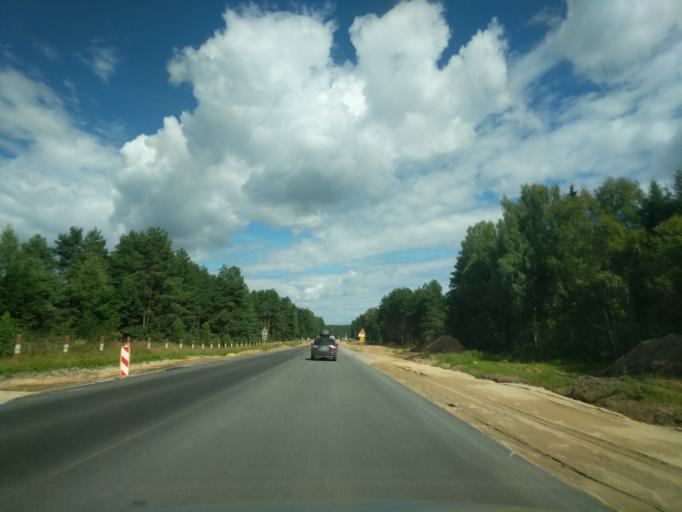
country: RU
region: Jaroslavl
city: Levashevo
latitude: 57.6651
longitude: 40.5737
